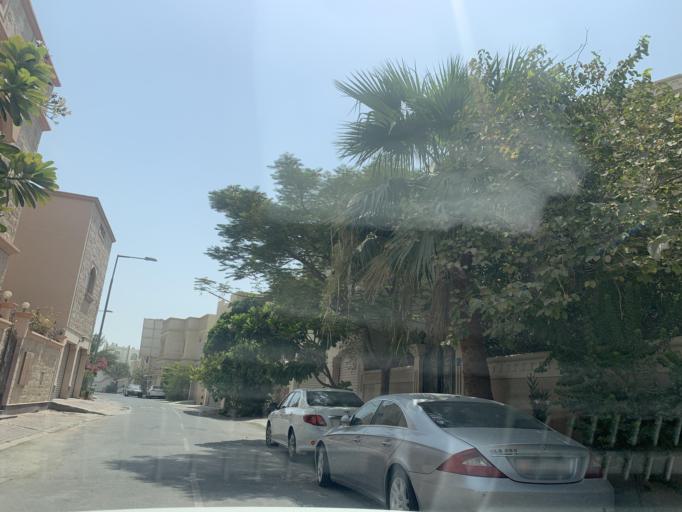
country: BH
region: Manama
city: Jidd Hafs
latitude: 26.2084
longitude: 50.5053
